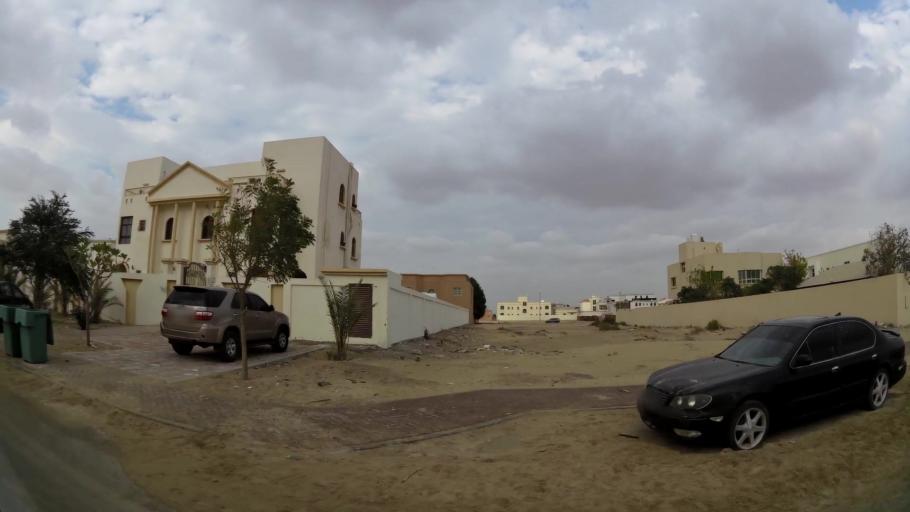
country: AE
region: Abu Dhabi
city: Abu Dhabi
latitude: 24.3436
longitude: 54.6148
